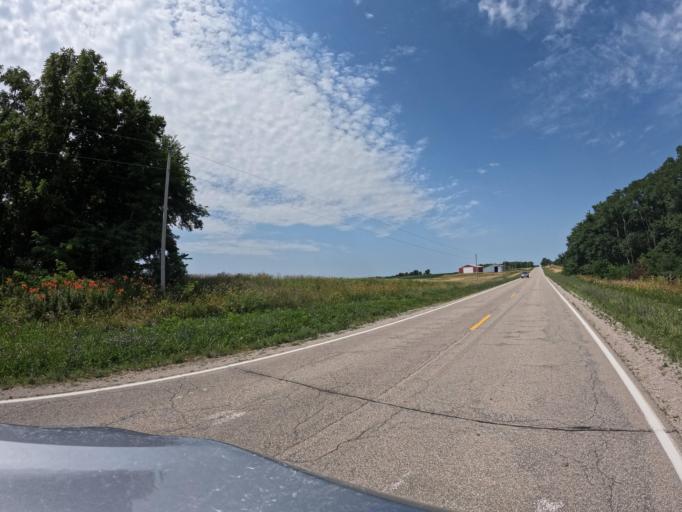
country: US
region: Iowa
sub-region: Appanoose County
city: Centerville
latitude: 40.8123
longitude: -92.9353
